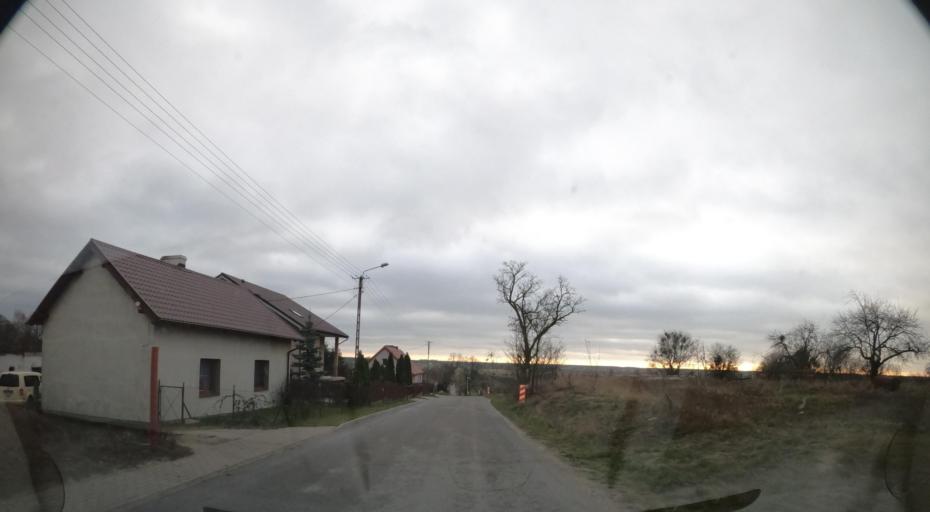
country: PL
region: Kujawsko-Pomorskie
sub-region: Powiat bydgoski
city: Sicienko
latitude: 53.1533
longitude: 17.8490
